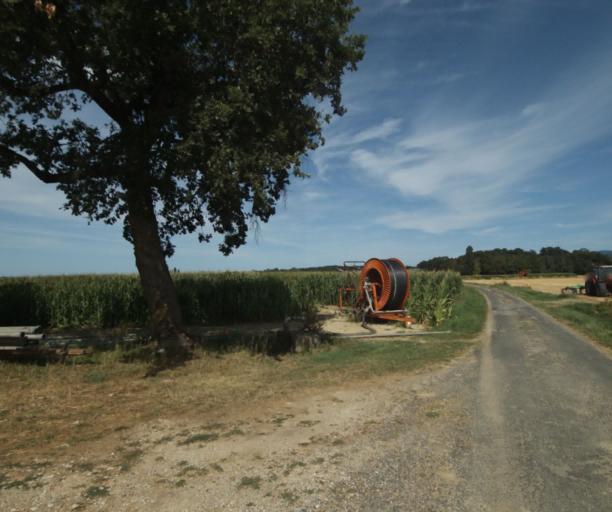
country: FR
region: Midi-Pyrenees
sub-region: Departement du Tarn
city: Soreze
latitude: 43.5099
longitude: 2.0774
